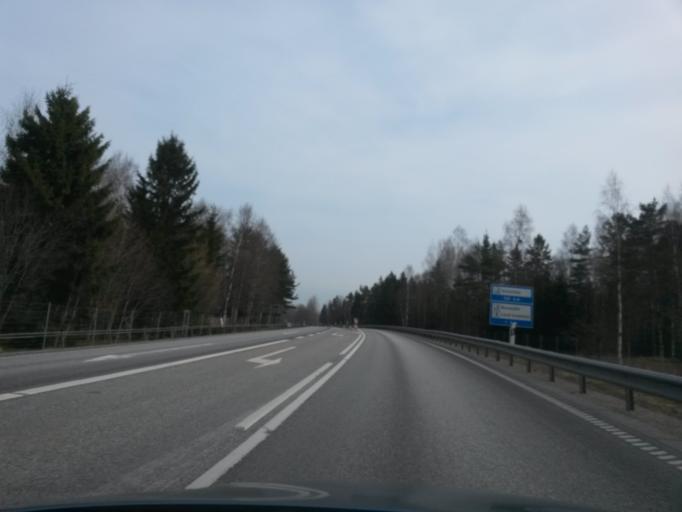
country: SE
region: OErebro
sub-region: Laxa Kommun
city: Laxa
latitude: 58.9610
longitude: 14.5303
